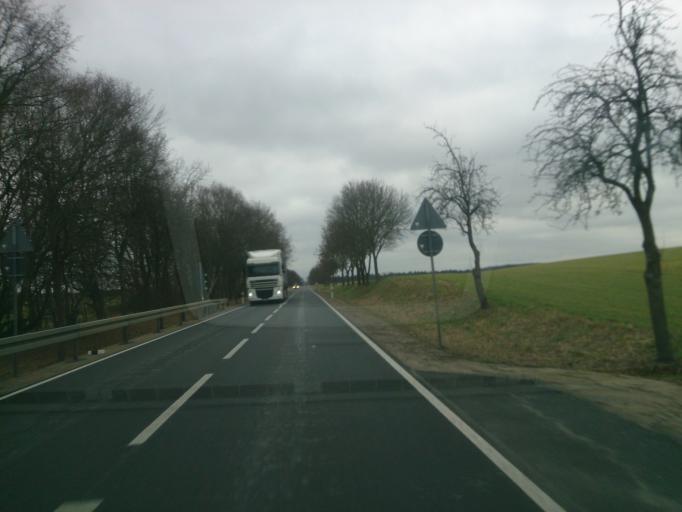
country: DE
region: Mecklenburg-Vorpommern
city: Mollenhagen
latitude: 53.6105
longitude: 12.8856
